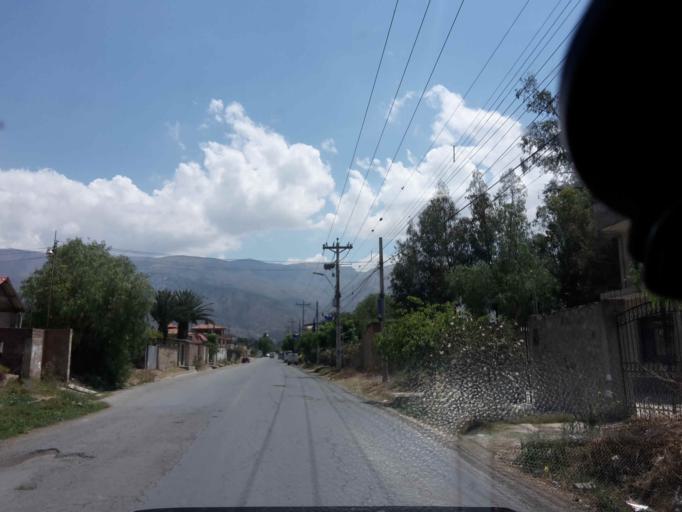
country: BO
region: Cochabamba
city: Cochabamba
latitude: -17.3601
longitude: -66.2287
